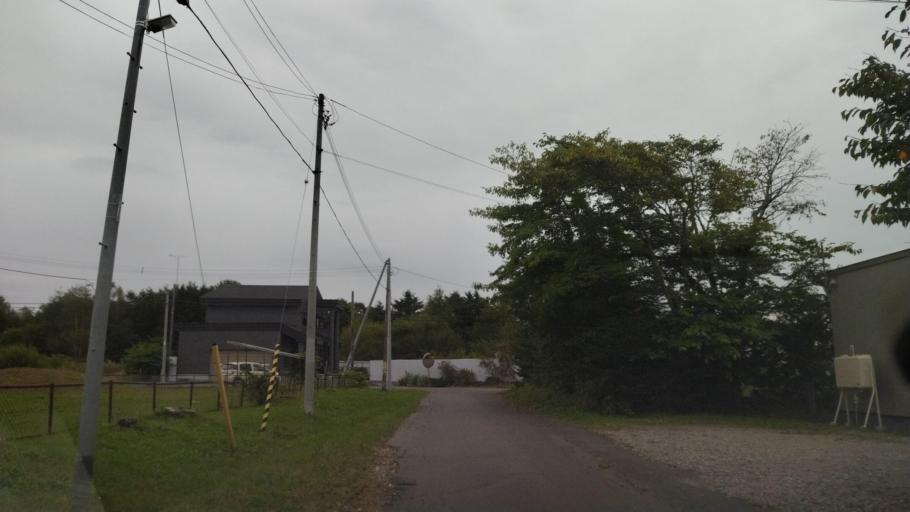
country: JP
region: Hokkaido
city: Otofuke
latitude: 43.2318
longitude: 143.2825
